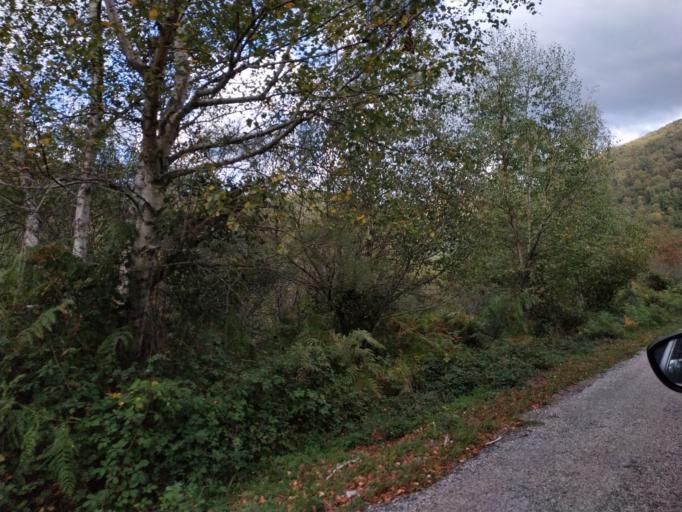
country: ES
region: Castille and Leon
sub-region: Provincia de Leon
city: Candin
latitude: 42.8643
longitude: -6.8588
